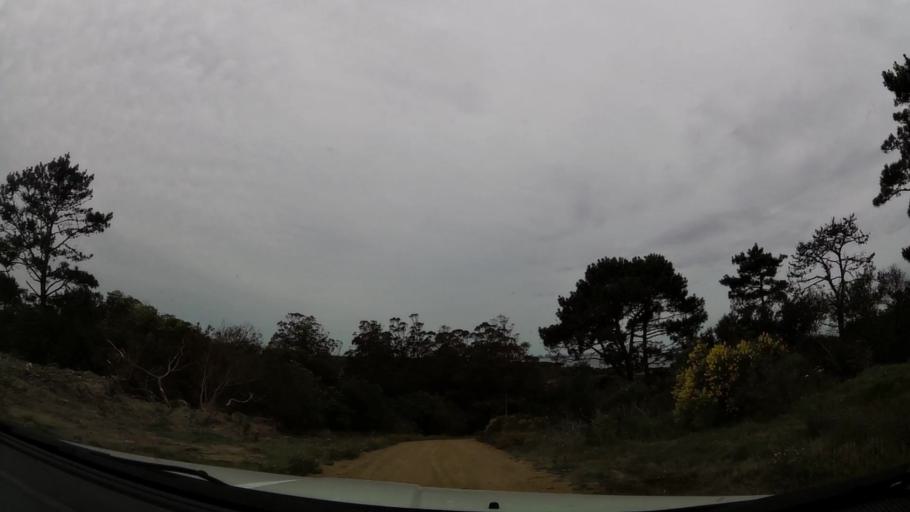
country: UY
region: Maldonado
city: Maldonado
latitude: -34.9024
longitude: -55.0404
